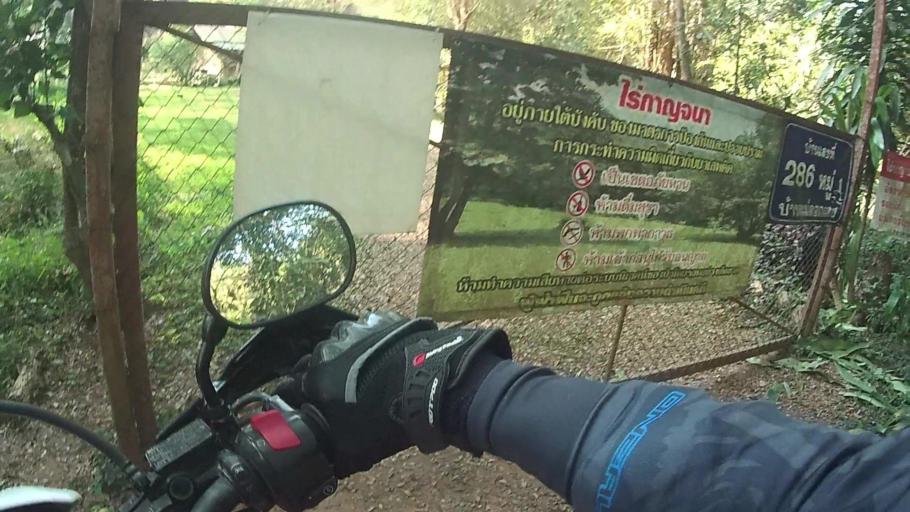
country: TH
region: Chiang Mai
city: San Sai
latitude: 18.9474
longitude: 99.1916
